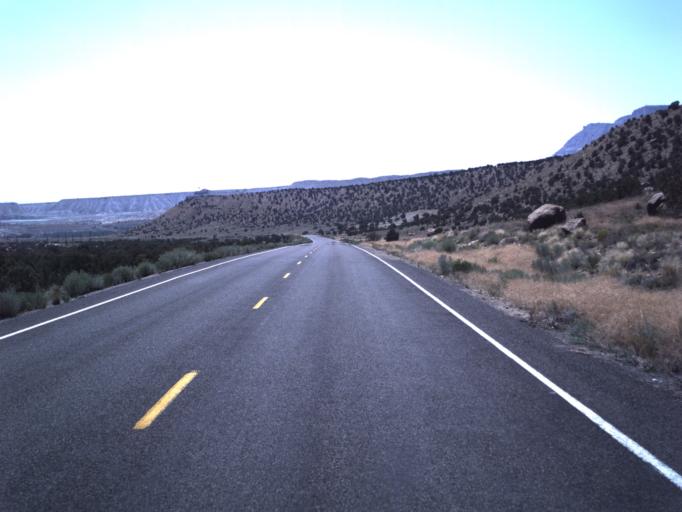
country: US
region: Utah
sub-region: Emery County
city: Orangeville
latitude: 39.2749
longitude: -111.1012
